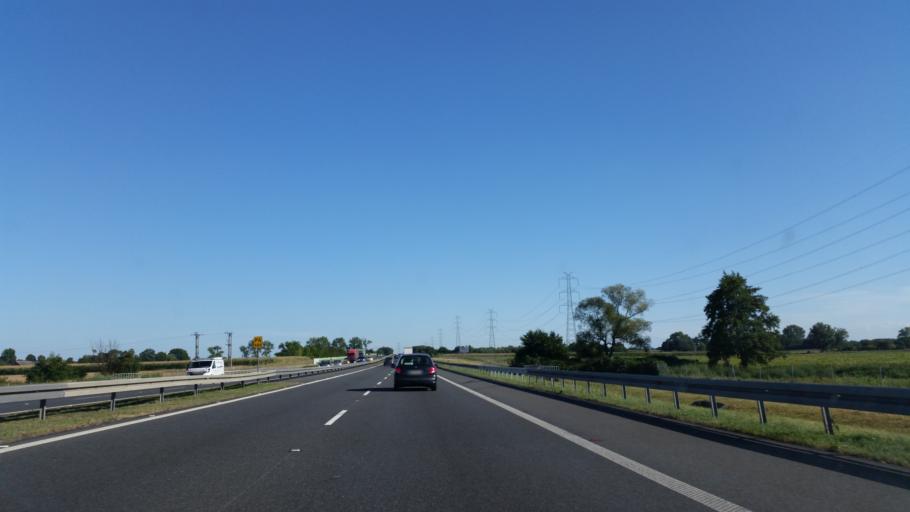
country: PL
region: Lower Silesian Voivodeship
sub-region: Powiat strzelinski
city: Wiazow
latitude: 50.8127
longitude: 17.3115
